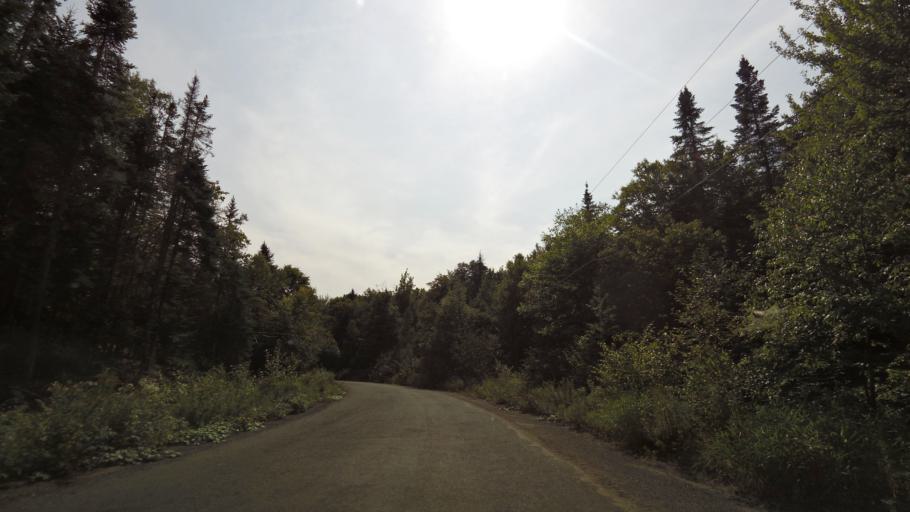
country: CA
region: New Brunswick
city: Hampton
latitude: 45.5761
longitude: -65.8317
